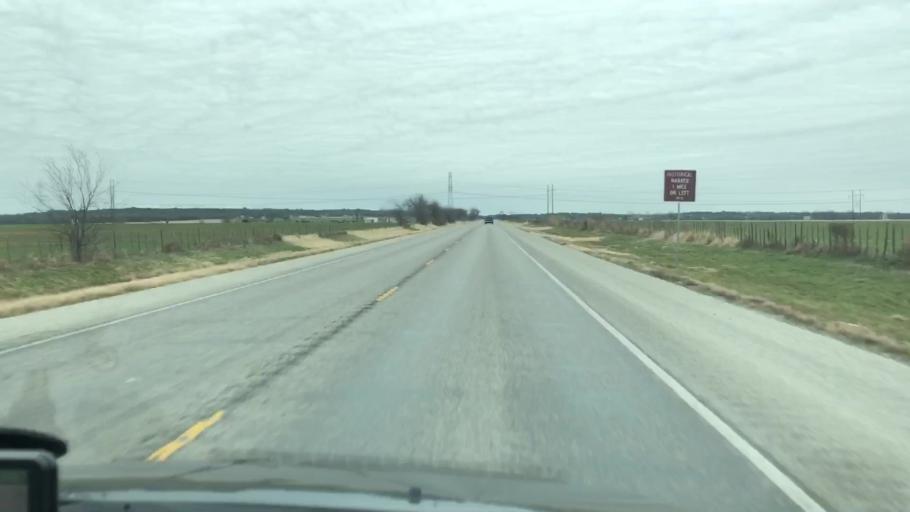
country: US
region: Texas
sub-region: Palo Pinto County
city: Mineral Wells
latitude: 32.9259
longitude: -98.0727
